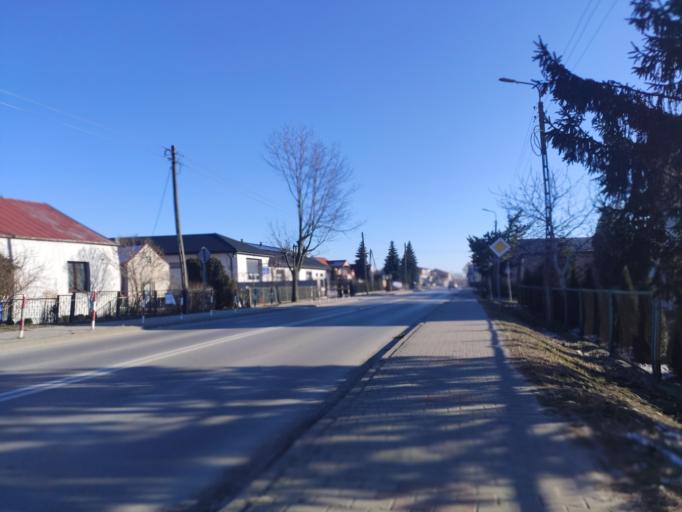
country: PL
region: Lublin Voivodeship
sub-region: Powiat lubartowski
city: Kock
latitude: 51.6412
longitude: 22.4480
